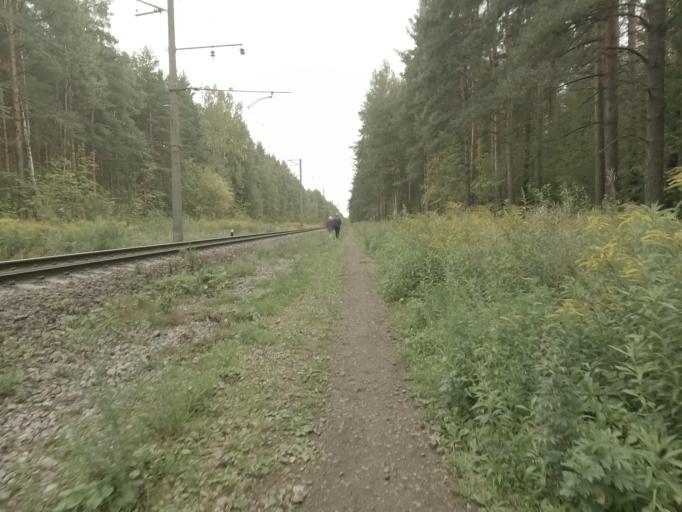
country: RU
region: St.-Petersburg
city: Krasnogvargeisky
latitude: 59.9664
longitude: 30.5121
